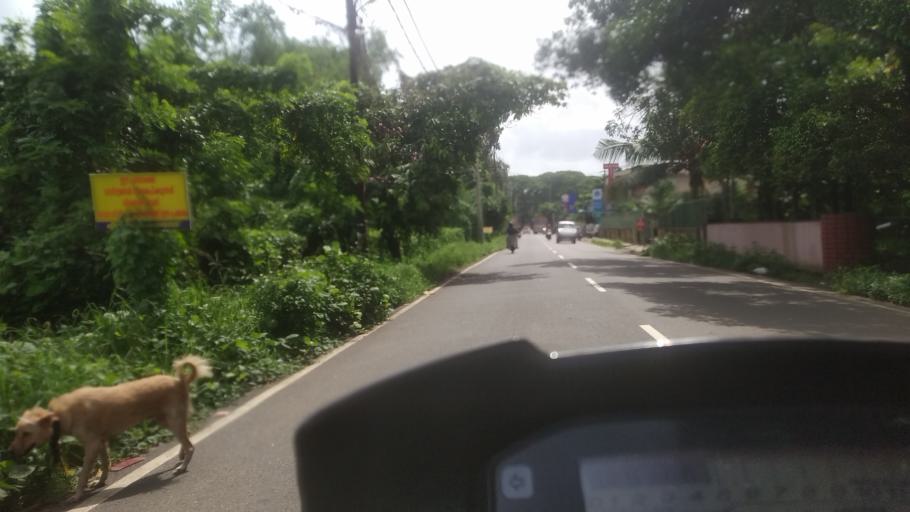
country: IN
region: Kerala
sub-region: Thrissur District
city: Kodungallur
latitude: 10.1477
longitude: 76.2471
